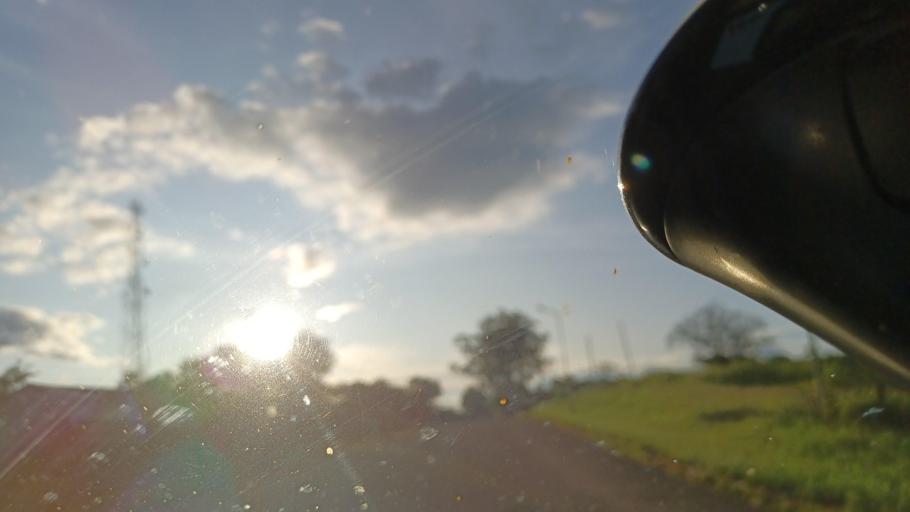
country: ZM
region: North-Western
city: Kasempa
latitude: -13.4589
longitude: 25.8353
